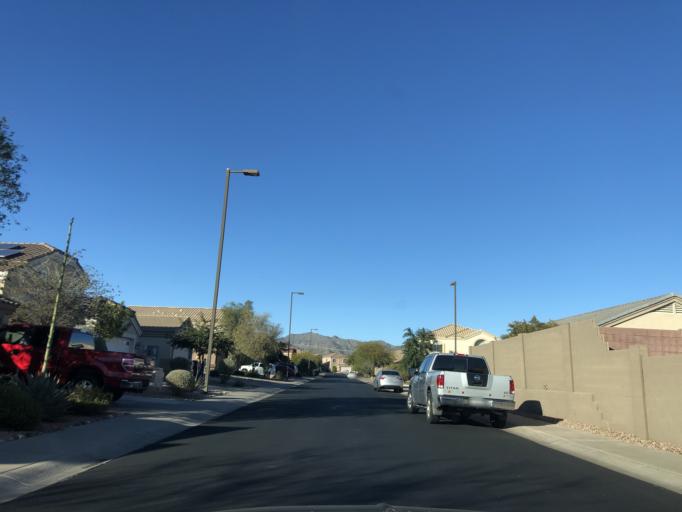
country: US
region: Arizona
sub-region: Maricopa County
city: Buckeye
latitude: 33.4372
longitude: -112.5667
